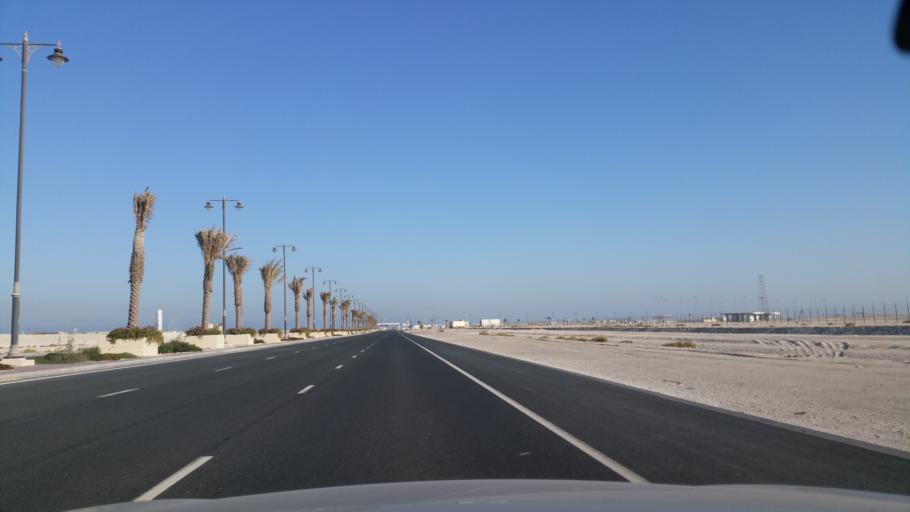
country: QA
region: Al Wakrah
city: Umm Sa'id
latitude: 25.0568
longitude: 51.5962
